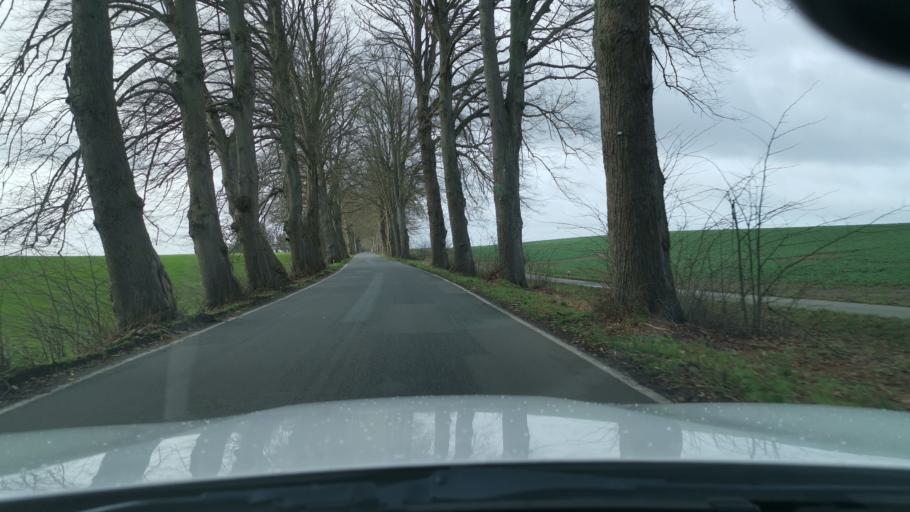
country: DE
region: Mecklenburg-Vorpommern
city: Wardow
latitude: 54.0005
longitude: 12.3851
